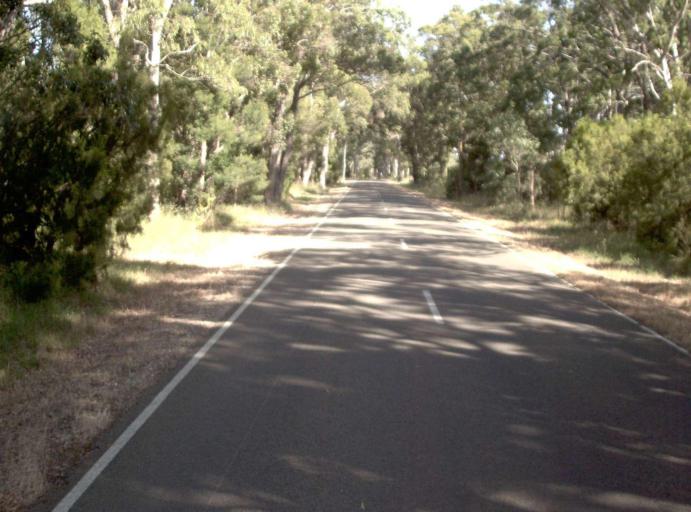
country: AU
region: Victoria
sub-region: East Gippsland
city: Lakes Entrance
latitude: -37.8032
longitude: 147.8379
